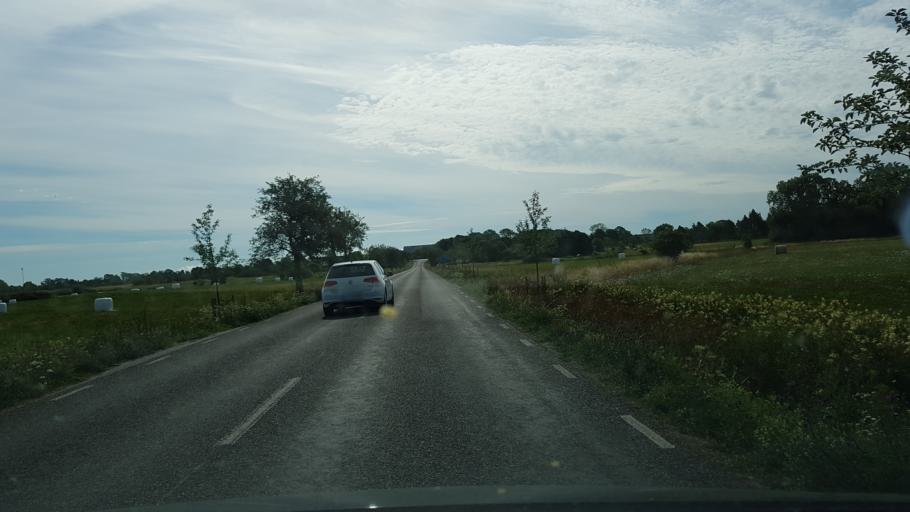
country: SE
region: Gotland
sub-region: Gotland
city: Hemse
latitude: 57.4311
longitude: 18.6227
